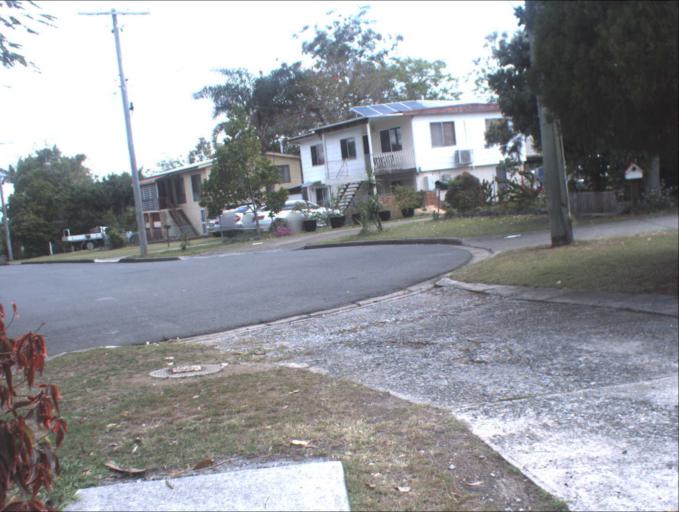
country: AU
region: Queensland
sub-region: Logan
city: Logan City
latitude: -27.6483
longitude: 153.1127
